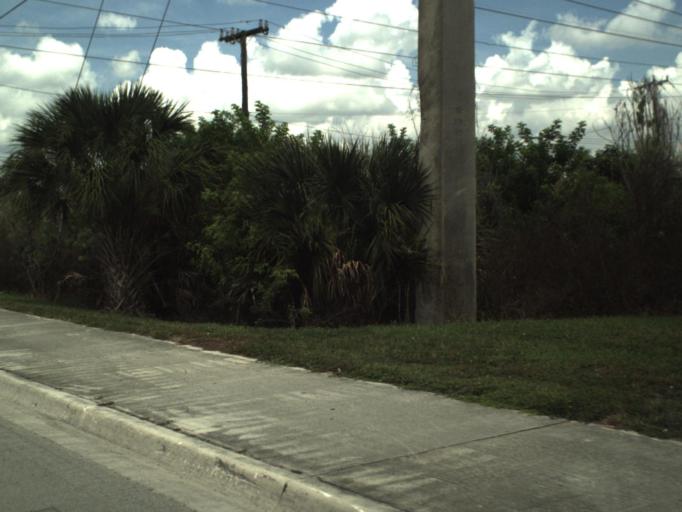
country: US
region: Florida
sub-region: Broward County
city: Davie
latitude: 26.0630
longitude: -80.2013
